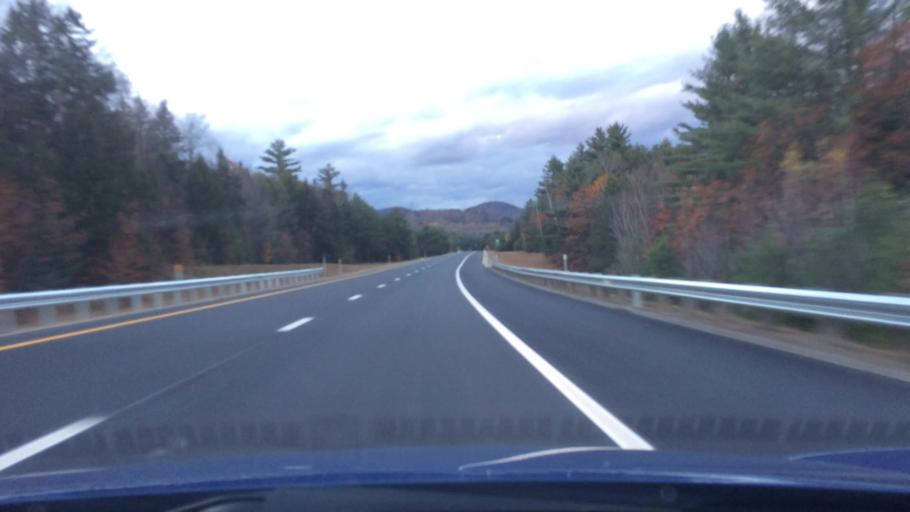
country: US
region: New Hampshire
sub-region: Grafton County
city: Thornton
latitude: 43.9084
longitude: -71.6907
